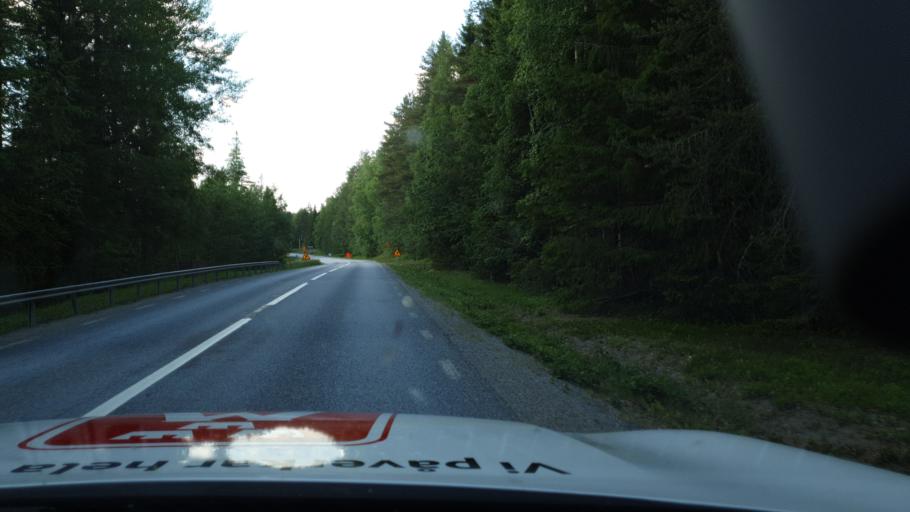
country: SE
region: Vaesterbotten
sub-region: Skelleftea Kommun
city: Burtraesk
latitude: 64.5083
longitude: 20.4960
